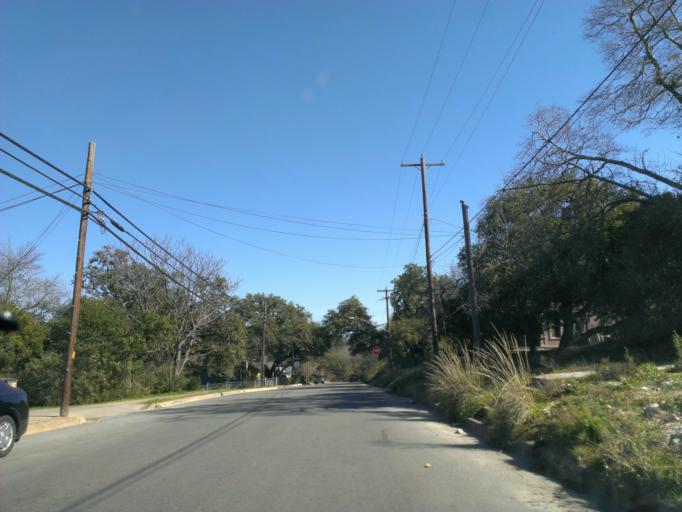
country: US
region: Texas
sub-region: Travis County
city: Austin
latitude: 30.2470
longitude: -97.7472
